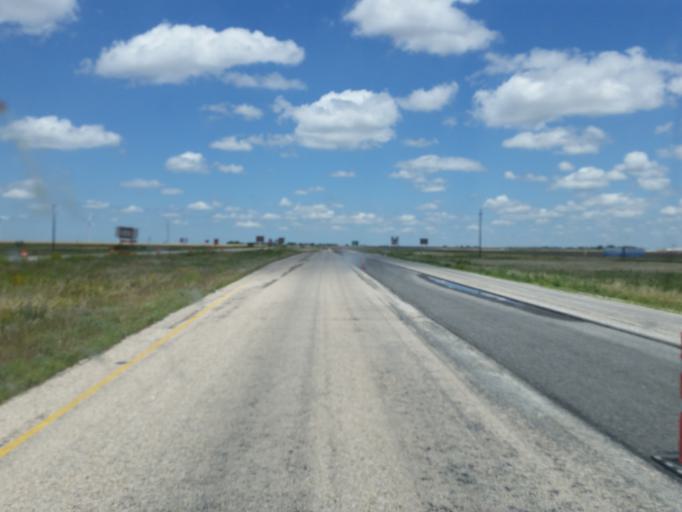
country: US
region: Texas
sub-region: Nolan County
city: Roscoe
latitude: 32.4548
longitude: -100.5424
